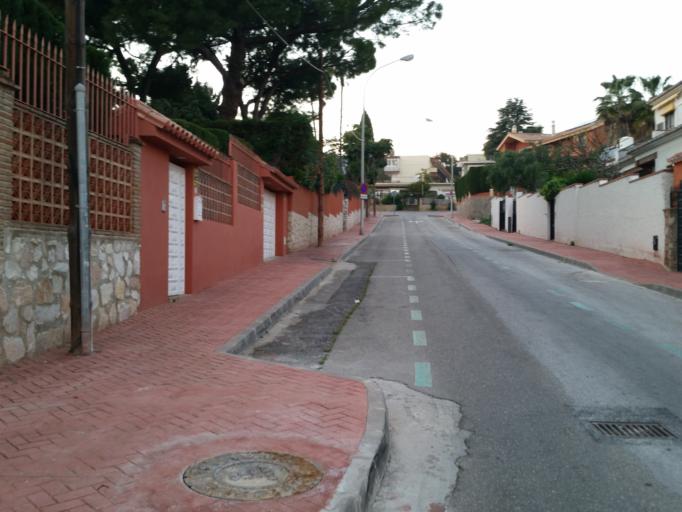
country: ES
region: Andalusia
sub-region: Provincia de Malaga
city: Torremolinos
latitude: 36.6011
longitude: -4.5205
